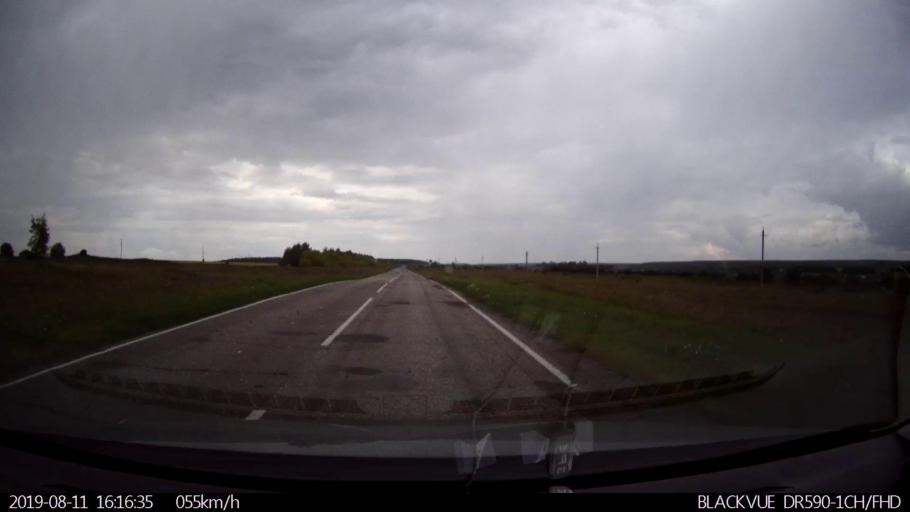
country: RU
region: Ulyanovsk
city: Mayna
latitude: 54.0422
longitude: 47.6206
